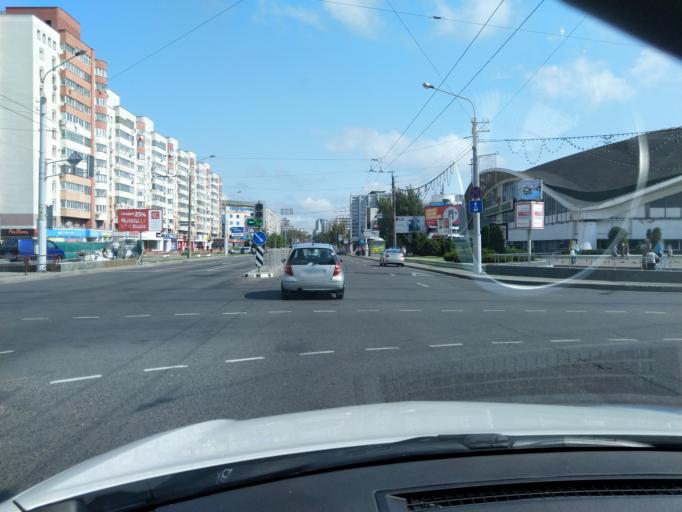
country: BY
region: Minsk
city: Minsk
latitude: 53.9194
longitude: 27.5753
